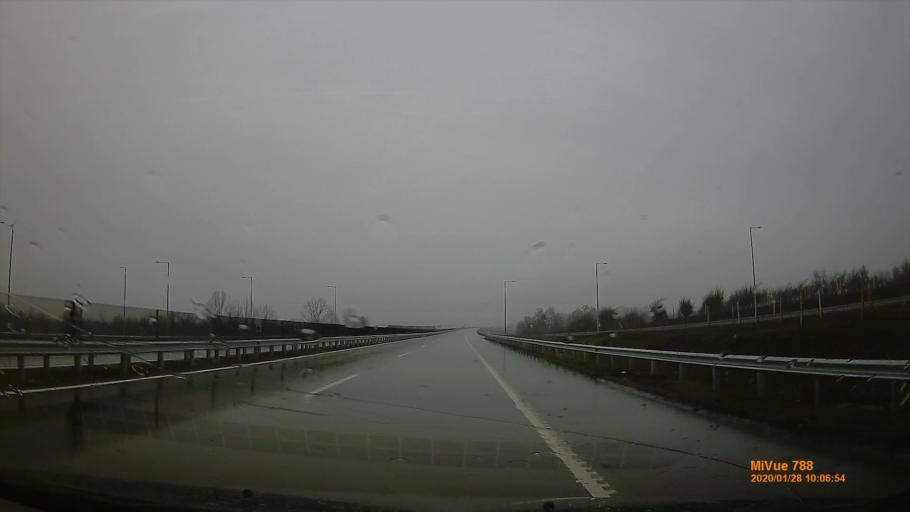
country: HU
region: Pest
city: Pilis
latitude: 47.2890
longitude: 19.5802
